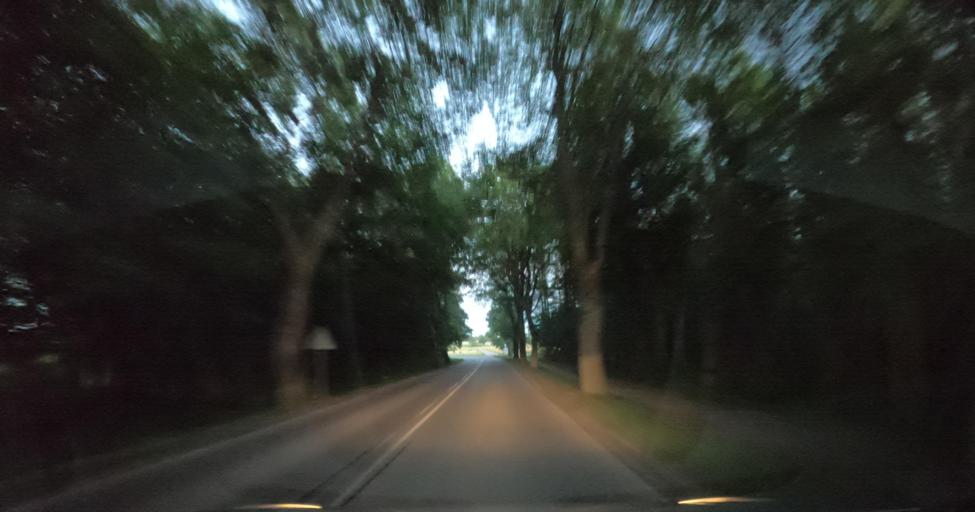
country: PL
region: Pomeranian Voivodeship
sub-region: Powiat wejherowski
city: Szemud
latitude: 54.4678
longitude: 18.2813
